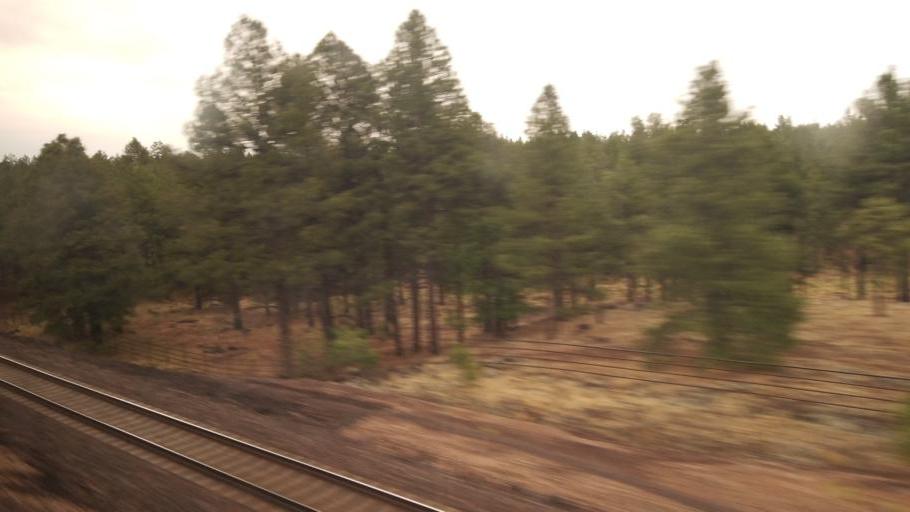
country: US
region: Arizona
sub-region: Coconino County
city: Parks
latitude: 35.2379
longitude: -111.9976
